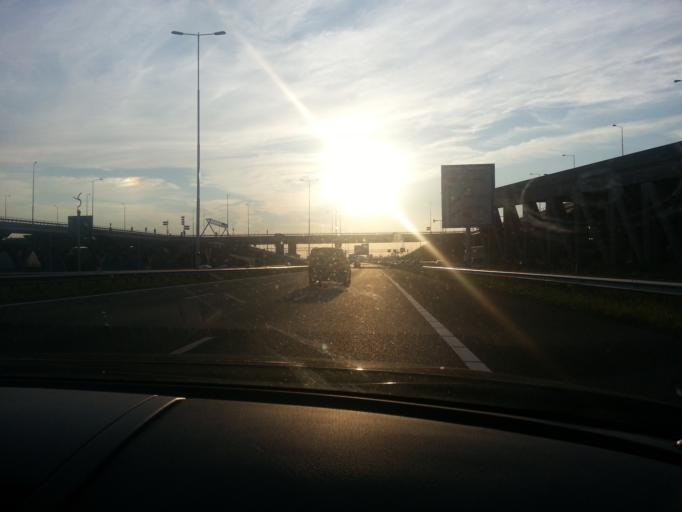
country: NL
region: South Holland
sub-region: Gemeente Albrandswaard
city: Rhoon
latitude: 51.8702
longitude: 4.4321
